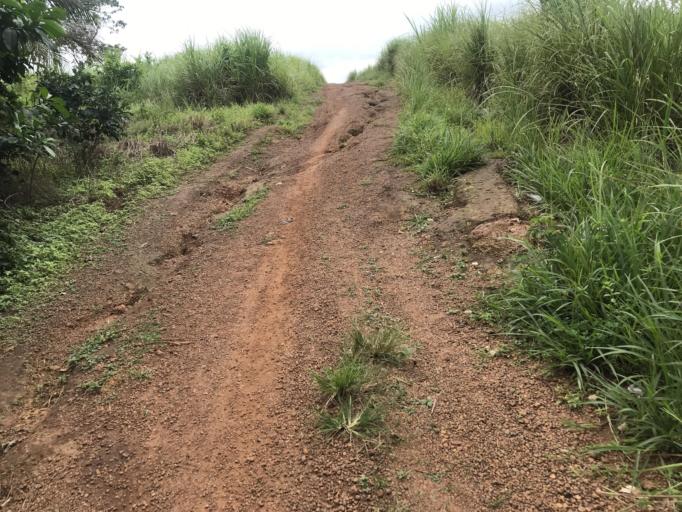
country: SL
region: Eastern Province
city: Buedu
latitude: 8.4699
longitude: -10.3294
